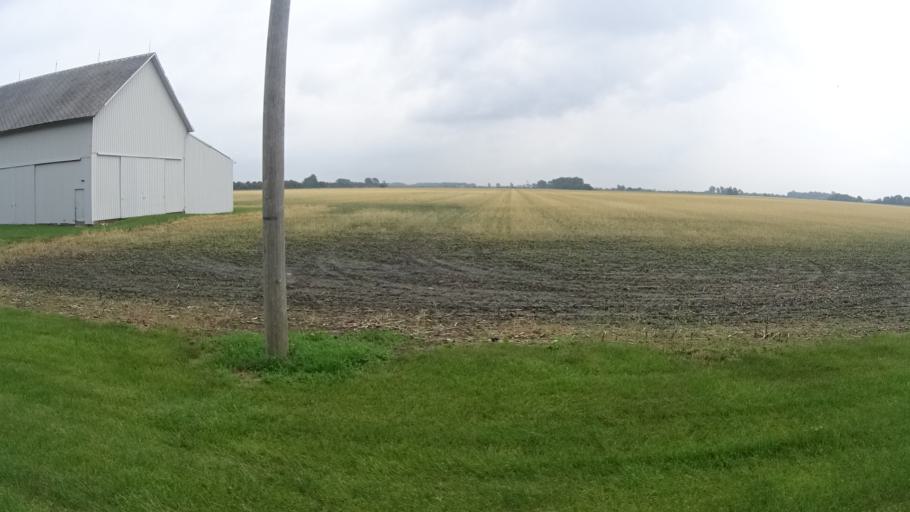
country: US
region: Ohio
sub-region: Huron County
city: Bellevue
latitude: 41.3133
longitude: -82.7928
